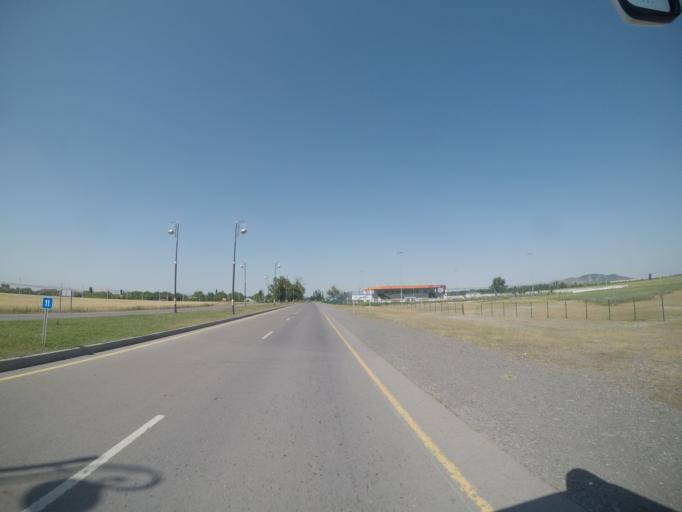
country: AZ
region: Qabala Rayon
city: Qutqashen
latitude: 40.8498
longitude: 47.7390
